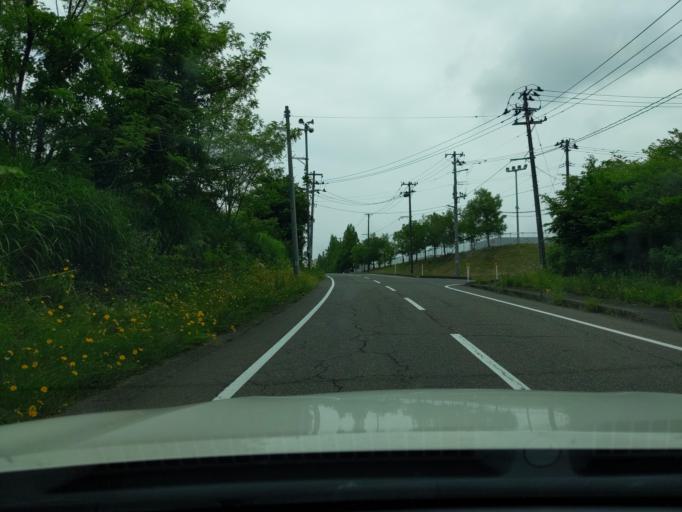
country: JP
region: Niigata
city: Kashiwazaki
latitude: 37.3427
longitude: 138.5962
